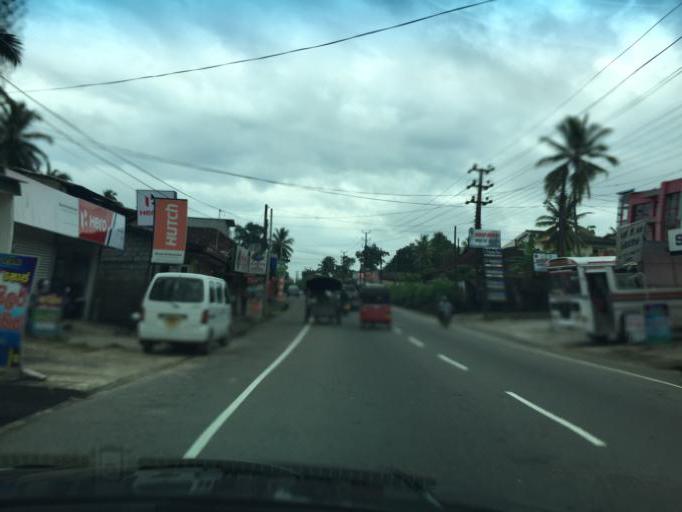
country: LK
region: Western
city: Horana South
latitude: 6.7189
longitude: 80.0702
